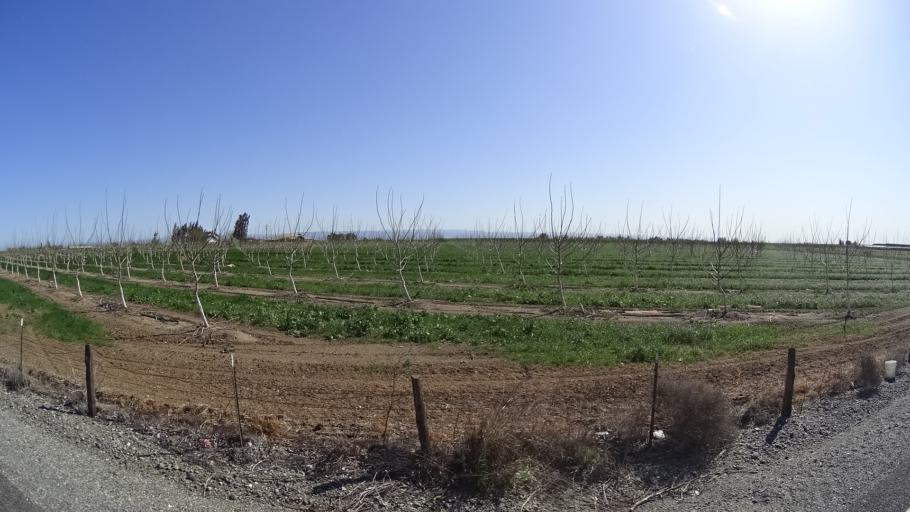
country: US
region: California
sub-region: Glenn County
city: Orland
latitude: 39.7801
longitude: -122.1161
